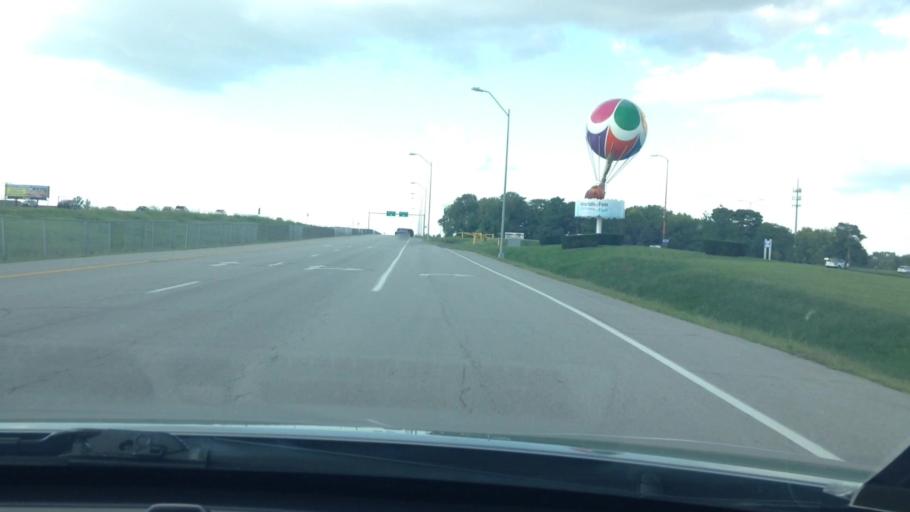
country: US
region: Missouri
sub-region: Clay County
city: Claycomo
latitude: 39.1752
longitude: -94.4921
